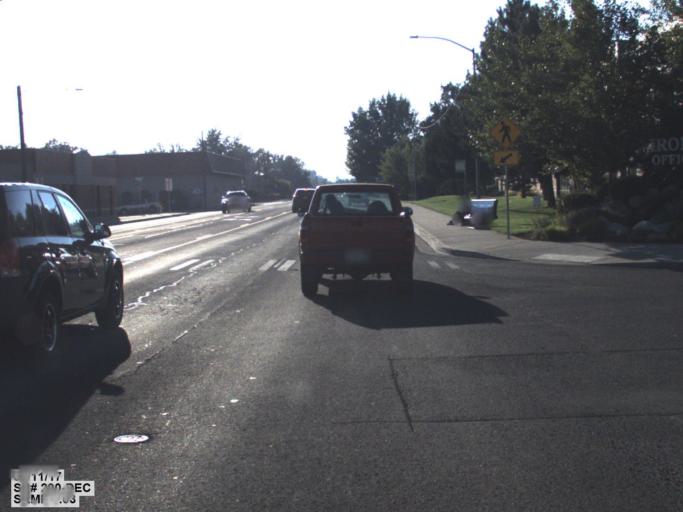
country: US
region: Washington
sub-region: Spokane County
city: Spokane
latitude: 47.6619
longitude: -117.3901
